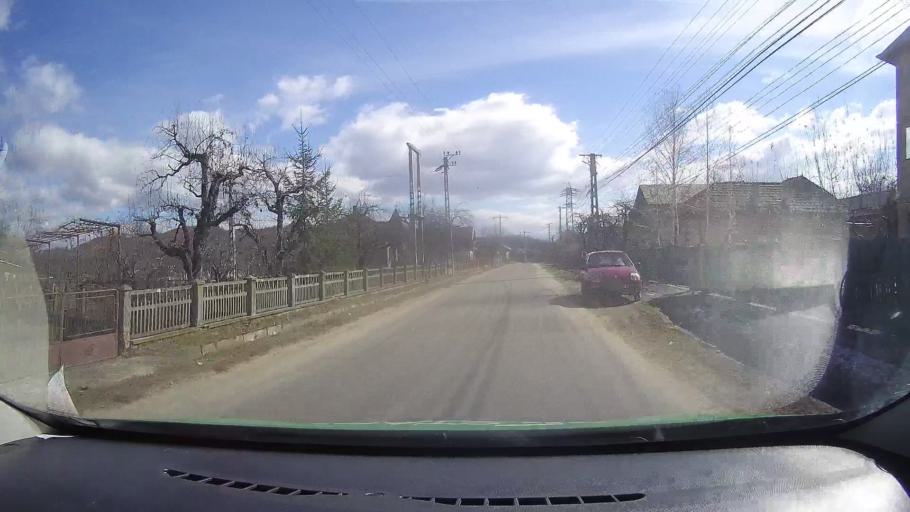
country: RO
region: Dambovita
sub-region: Comuna Branesti
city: Branesti
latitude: 45.0332
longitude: 25.4145
